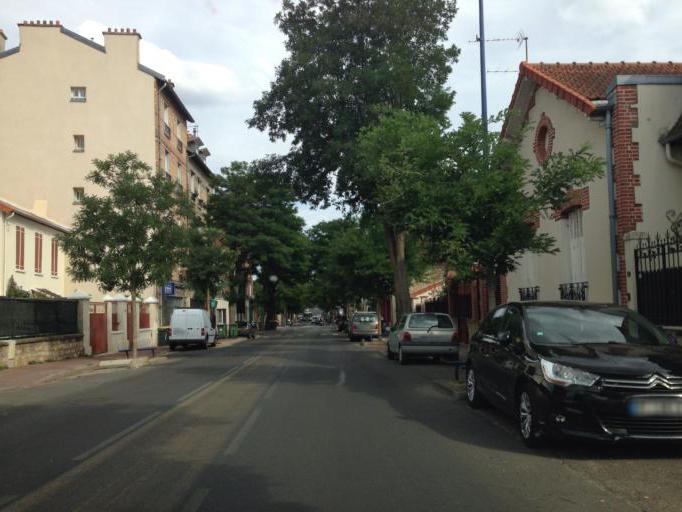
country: FR
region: Ile-de-France
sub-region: Departement des Hauts-de-Seine
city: Clamart
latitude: 48.8071
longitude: 2.2534
